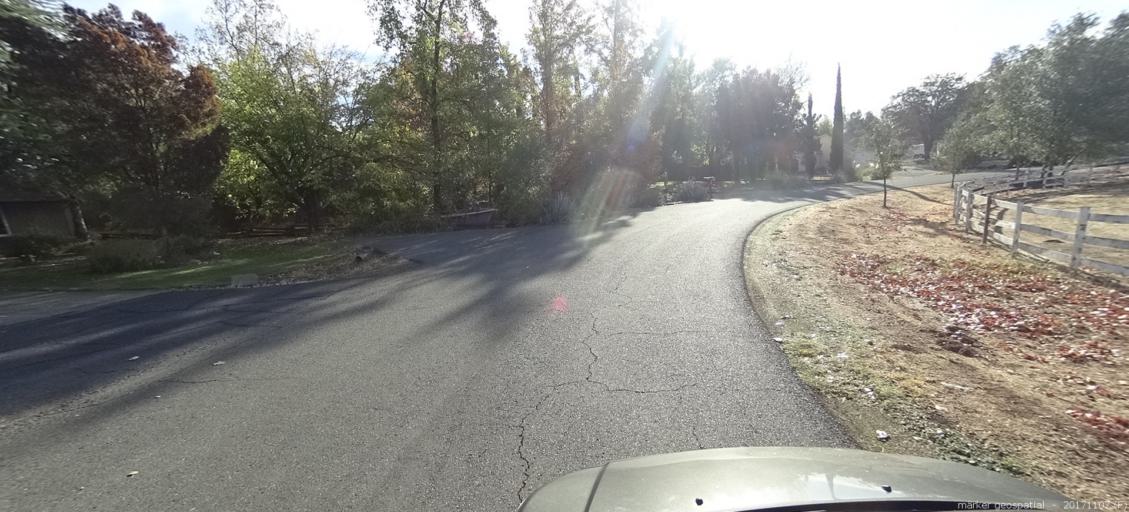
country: US
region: California
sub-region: Shasta County
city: Shasta
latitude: 40.5443
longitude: -122.4599
